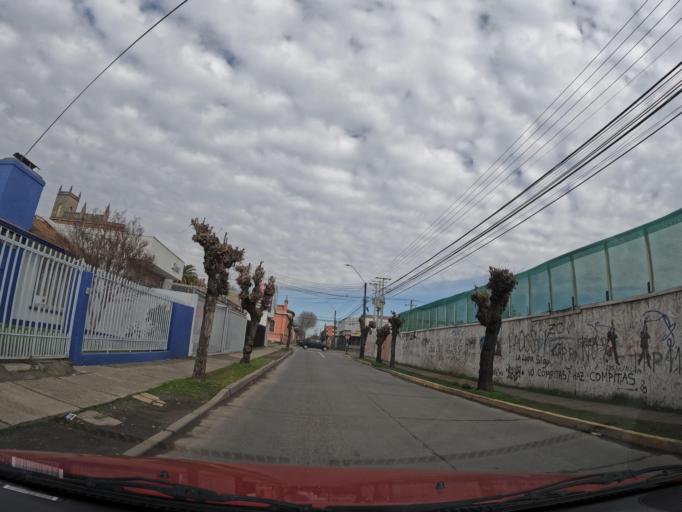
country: CL
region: Maule
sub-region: Provincia de Linares
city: Linares
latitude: -35.8461
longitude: -71.6023
